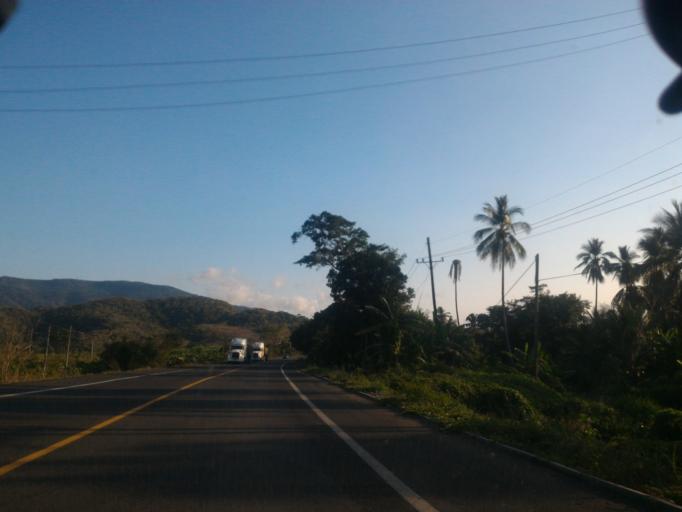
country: MX
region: Michoacan
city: Coahuayana Viejo
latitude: 18.6610
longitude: -103.6699
